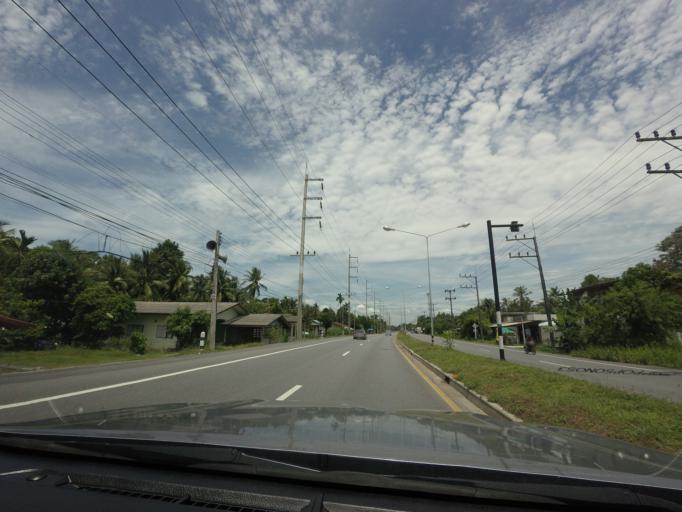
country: TH
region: Songkhla
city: Krasae Sin
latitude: 7.5751
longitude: 100.4092
